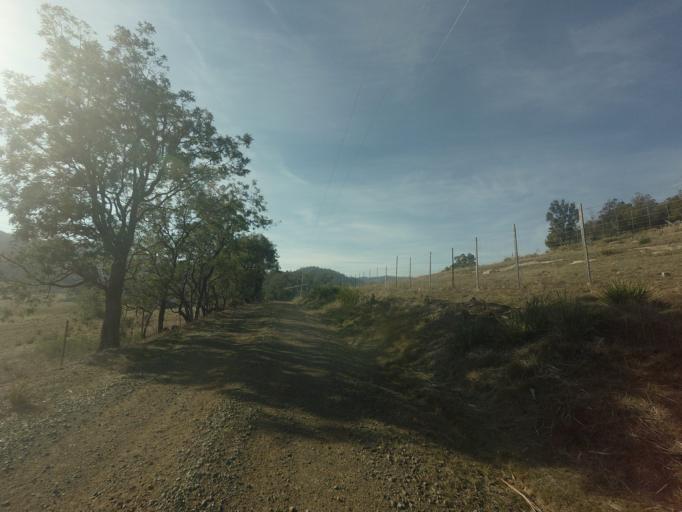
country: AU
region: Tasmania
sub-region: Sorell
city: Sorell
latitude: -42.5338
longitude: 147.4365
